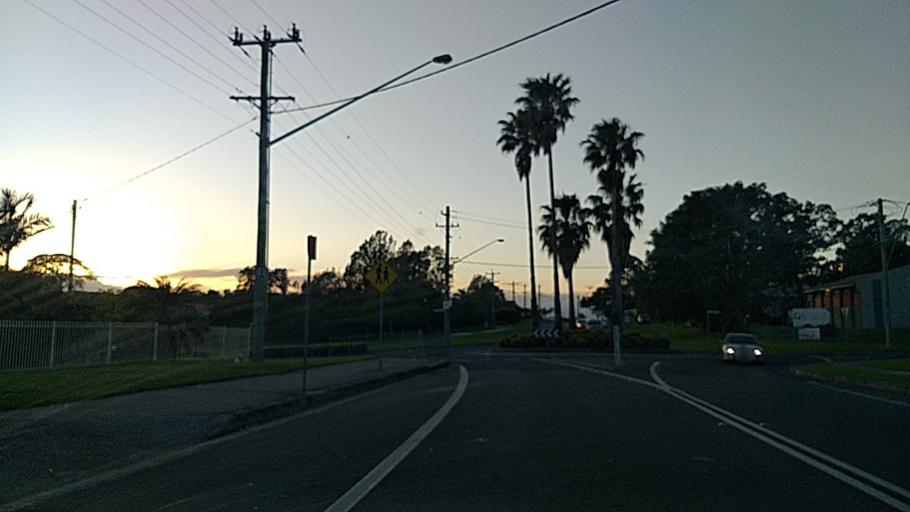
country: AU
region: New South Wales
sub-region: Wollongong
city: Koonawarra
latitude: -34.4934
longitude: 150.8170
